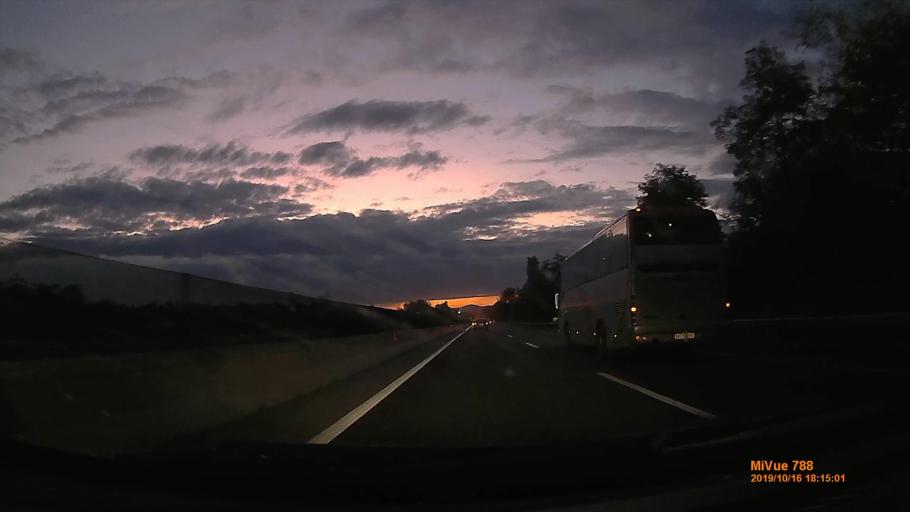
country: HU
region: Pest
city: Mogyorod
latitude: 47.6013
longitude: 19.2647
